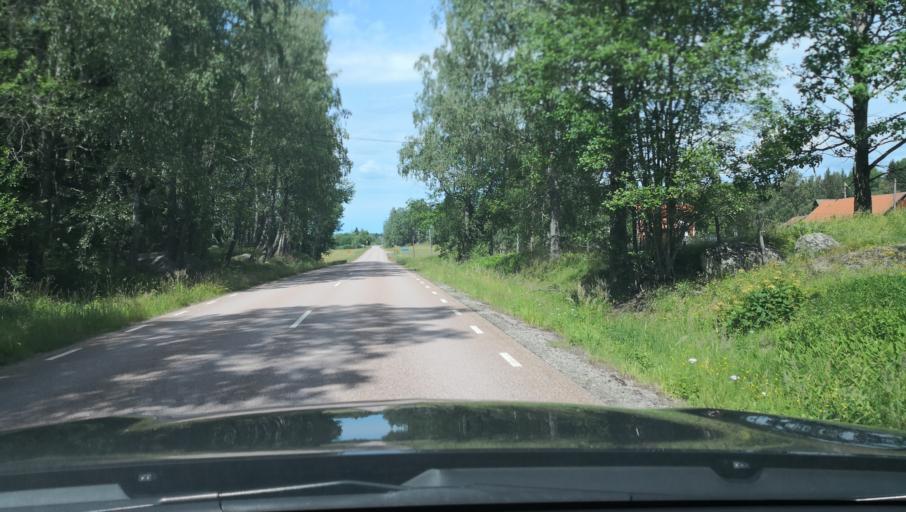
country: SE
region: Vaestmanland
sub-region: Surahammars Kommun
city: Ramnas
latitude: 59.8655
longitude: 16.0868
